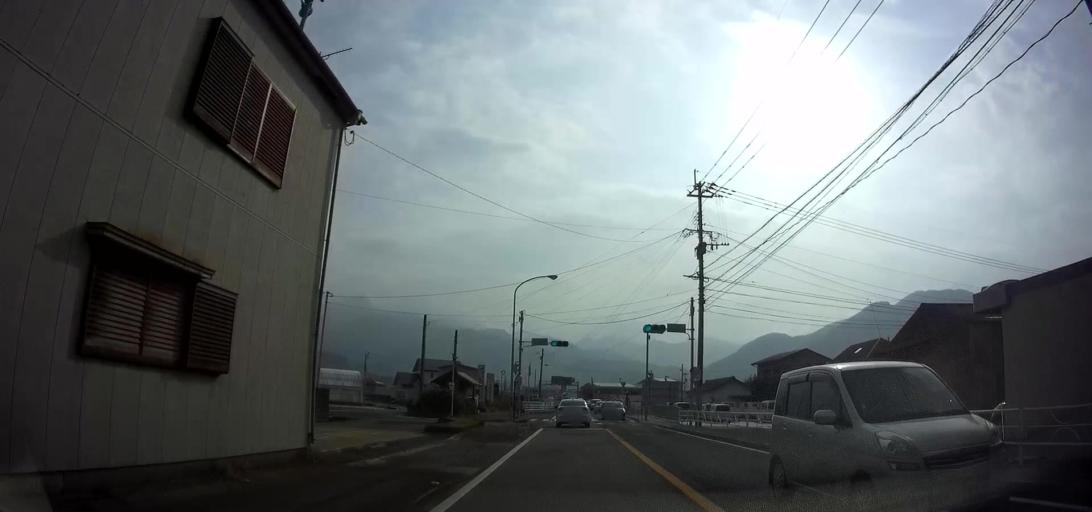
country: JP
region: Nagasaki
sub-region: Isahaya-shi
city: Isahaya
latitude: 32.7895
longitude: 130.1884
